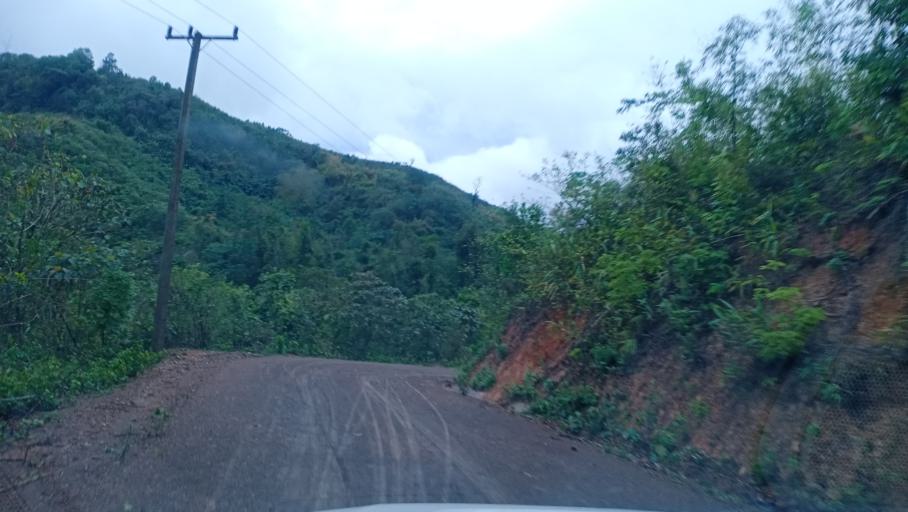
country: LA
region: Phongsali
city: Khoa
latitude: 21.2850
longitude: 102.6984
